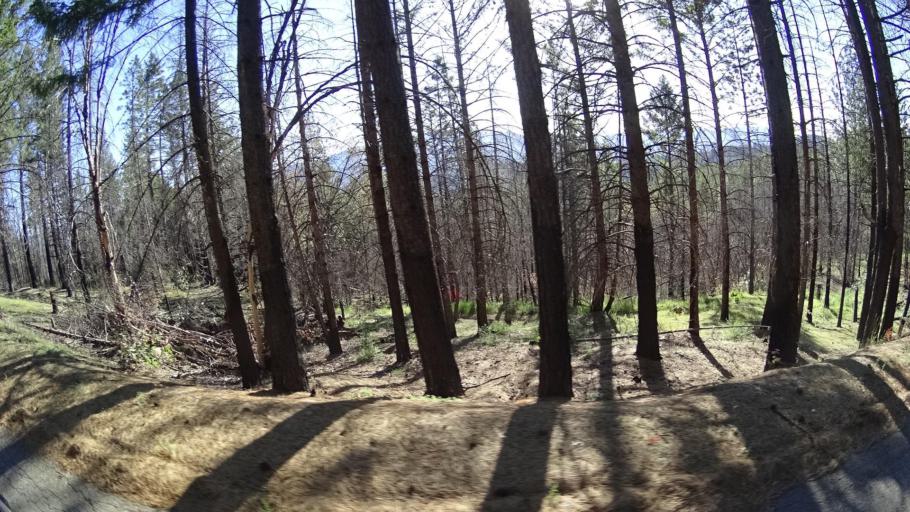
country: US
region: California
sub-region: Lake County
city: Upper Lake
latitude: 39.3091
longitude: -122.9390
